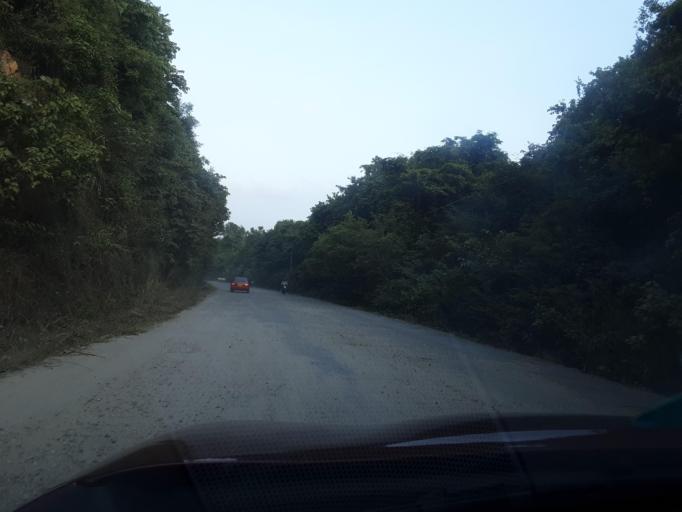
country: LK
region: Central
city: Dambulla
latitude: 7.8101
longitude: 80.7721
